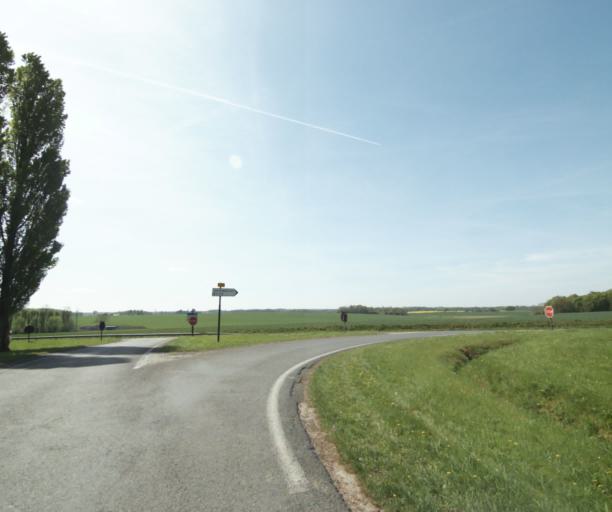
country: FR
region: Ile-de-France
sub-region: Departement de Seine-et-Marne
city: Nangis
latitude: 48.5462
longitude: 3.0163
